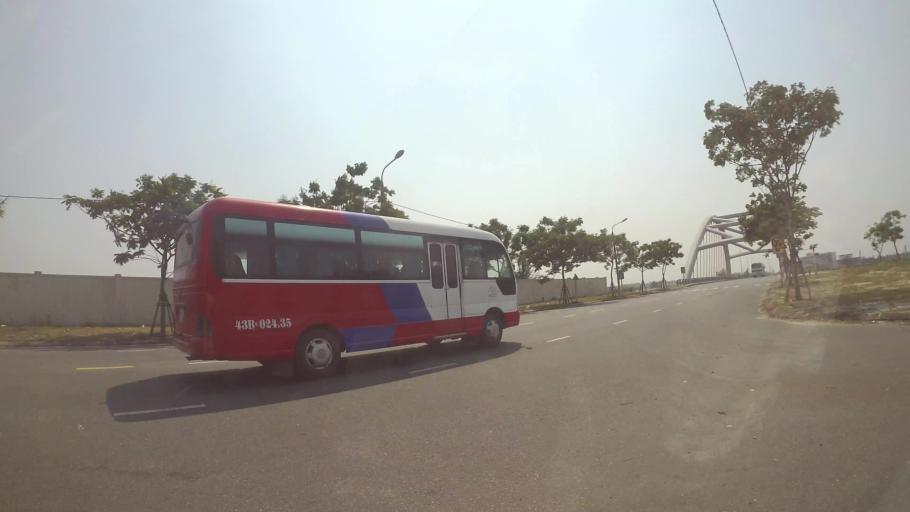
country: VN
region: Da Nang
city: Ngu Hanh Son
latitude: 15.9782
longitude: 108.2695
